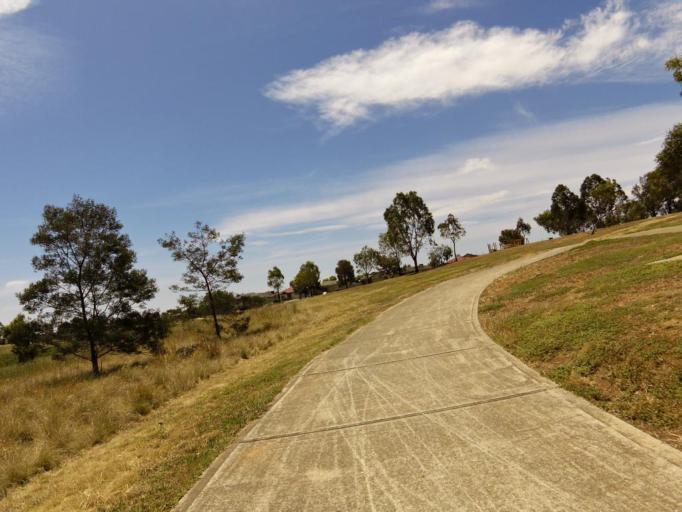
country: AU
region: Victoria
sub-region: Wyndham
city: Williams Landing
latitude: -37.8596
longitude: 144.7193
